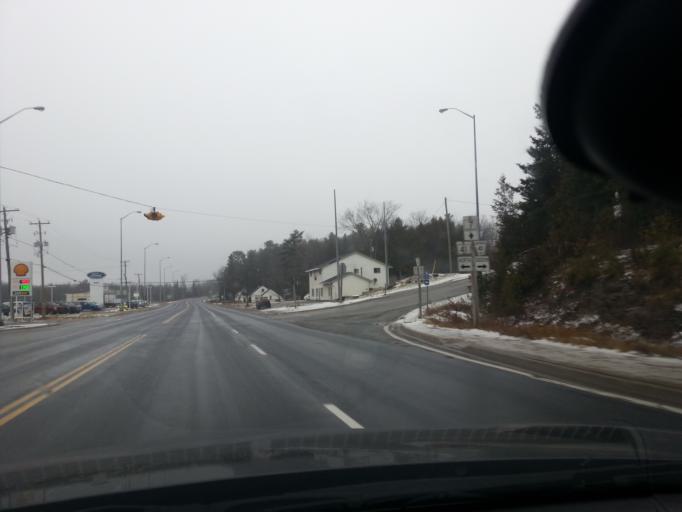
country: CA
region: Ontario
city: Greater Napanee
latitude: 44.6475
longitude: -77.1218
